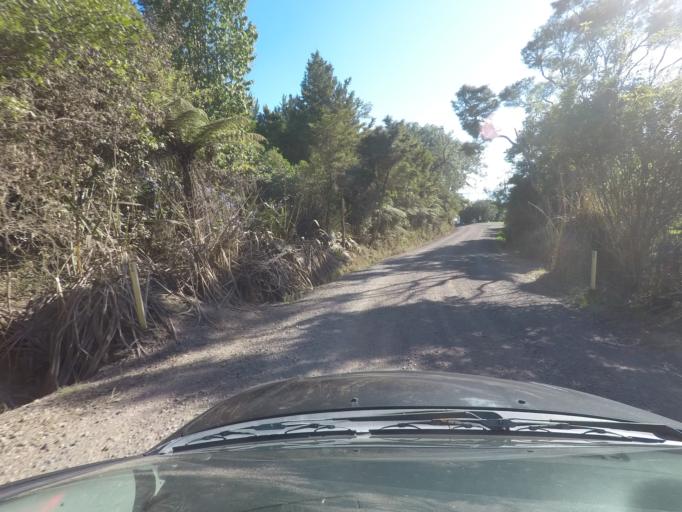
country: NZ
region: Northland
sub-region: Far North District
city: Paihia
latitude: -35.2548
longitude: 174.0711
